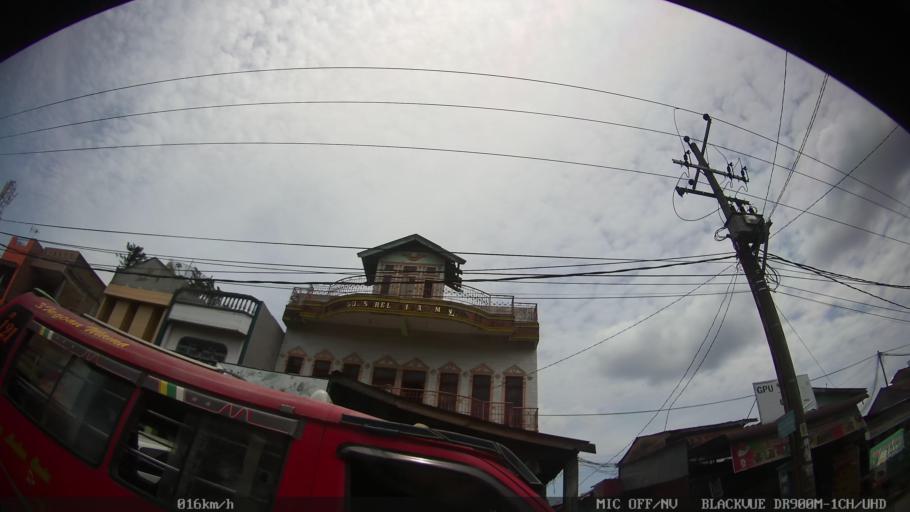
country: ID
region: North Sumatra
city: Deli Tua
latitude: 3.5398
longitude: 98.6534
